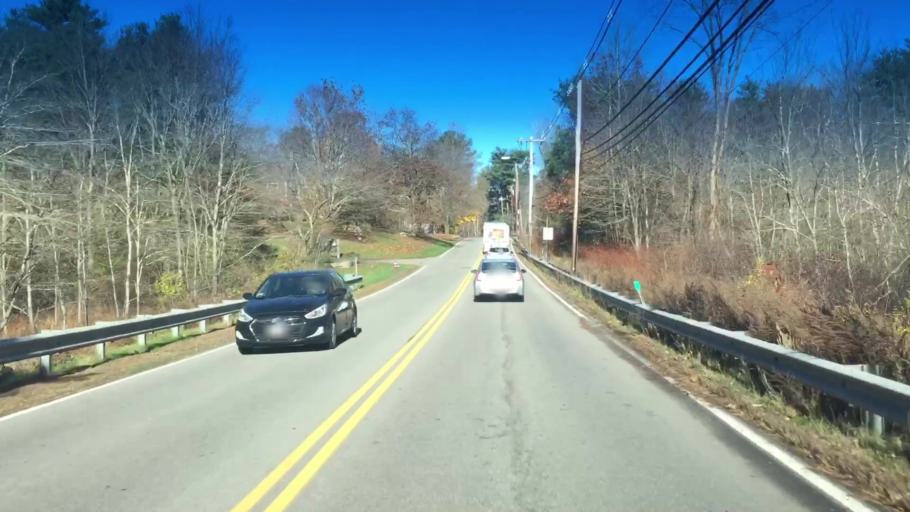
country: US
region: Massachusetts
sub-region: Norfolk County
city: Medfield
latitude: 42.1750
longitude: -71.2993
